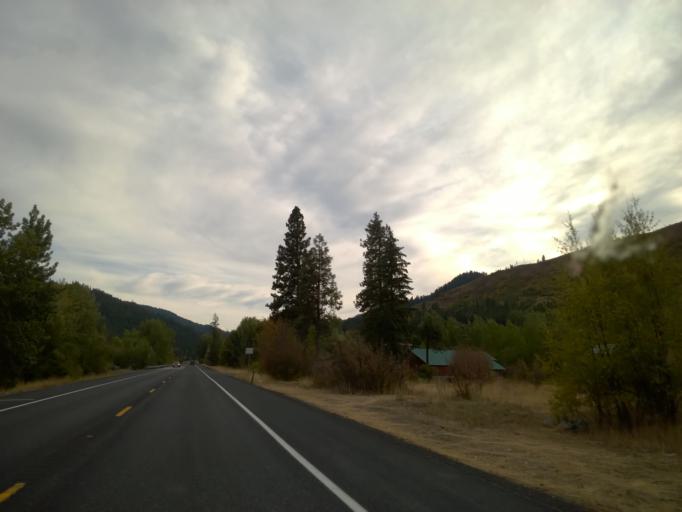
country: US
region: Washington
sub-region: Chelan County
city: Leavenworth
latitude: 47.5239
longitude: -120.6248
